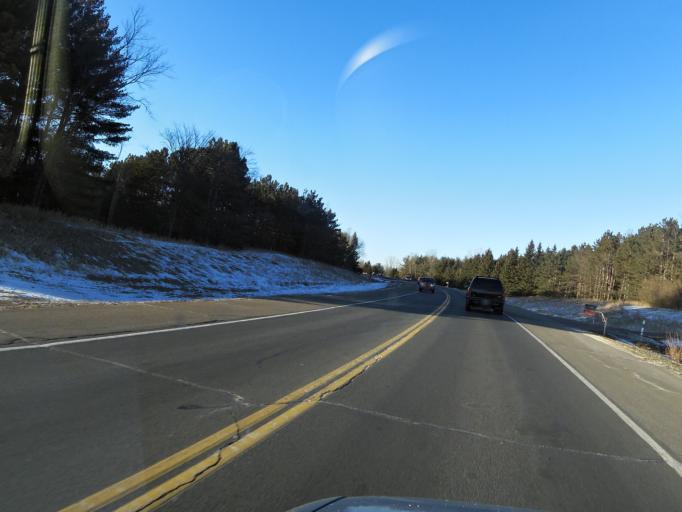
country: US
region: Minnesota
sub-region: Washington County
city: Lake Elmo
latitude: 44.9706
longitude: -92.8551
